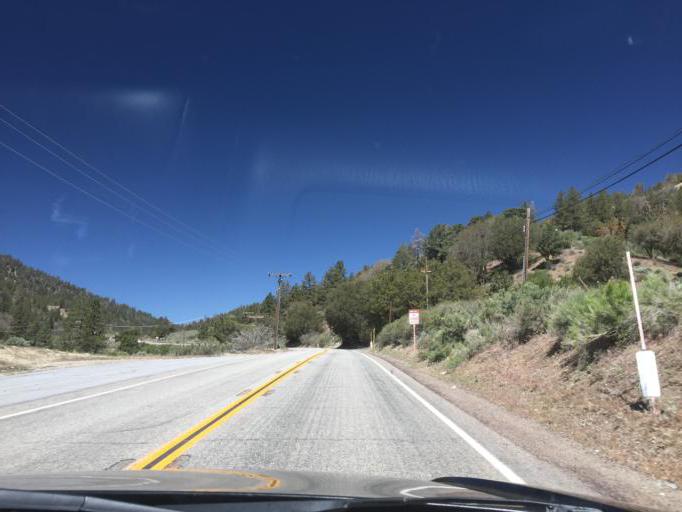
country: US
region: California
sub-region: San Bernardino County
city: Wrightwood
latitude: 34.3703
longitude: -117.6655
